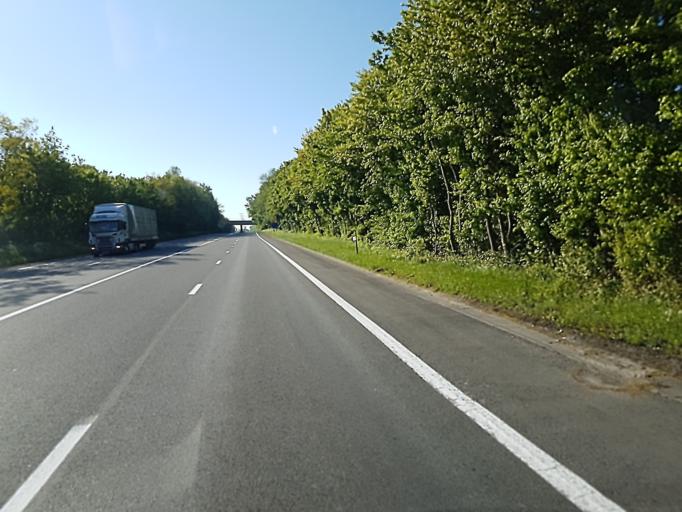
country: BE
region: Wallonia
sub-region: Province du Hainaut
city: Mouscron
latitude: 50.7618
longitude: 3.1981
